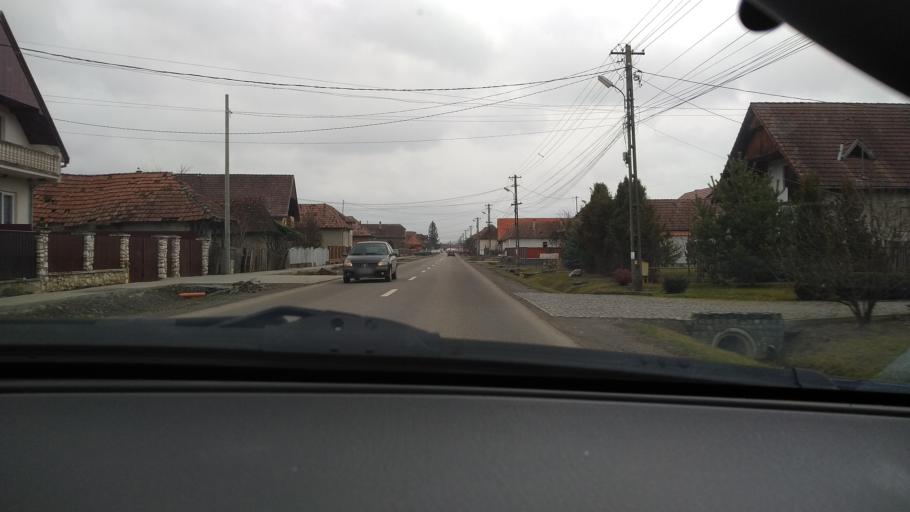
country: RO
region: Mures
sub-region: Comuna Miercurea Nirajului
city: Miercurea Nirajului
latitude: 46.5426
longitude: 24.8257
